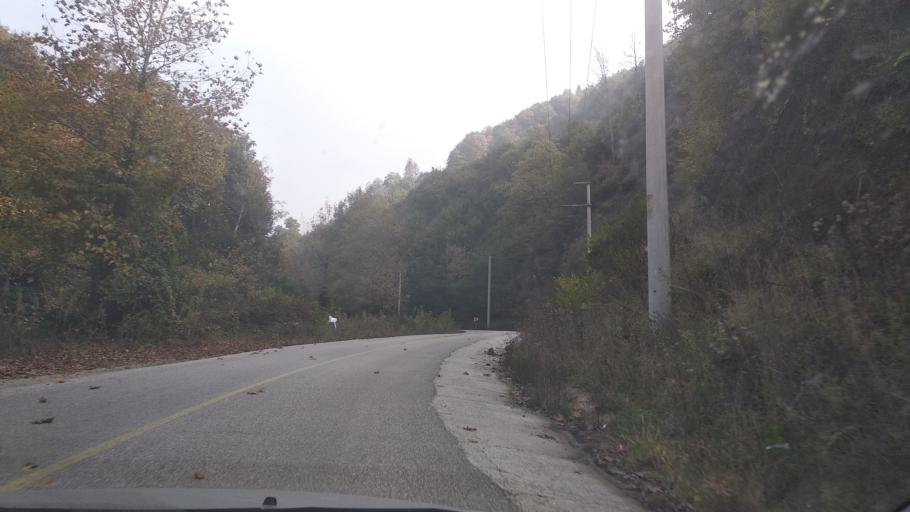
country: TR
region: Duzce
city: Kaynasli
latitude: 40.7337
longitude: 31.2208
